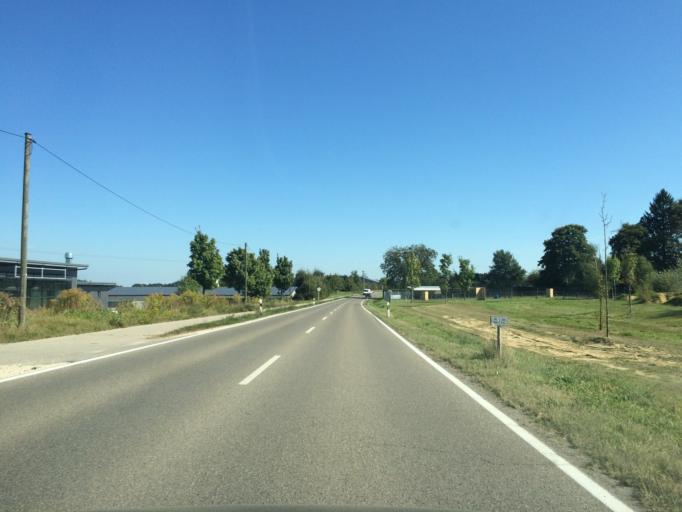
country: DE
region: Bavaria
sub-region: Swabia
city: Friedberg
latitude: 48.3479
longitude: 11.0002
